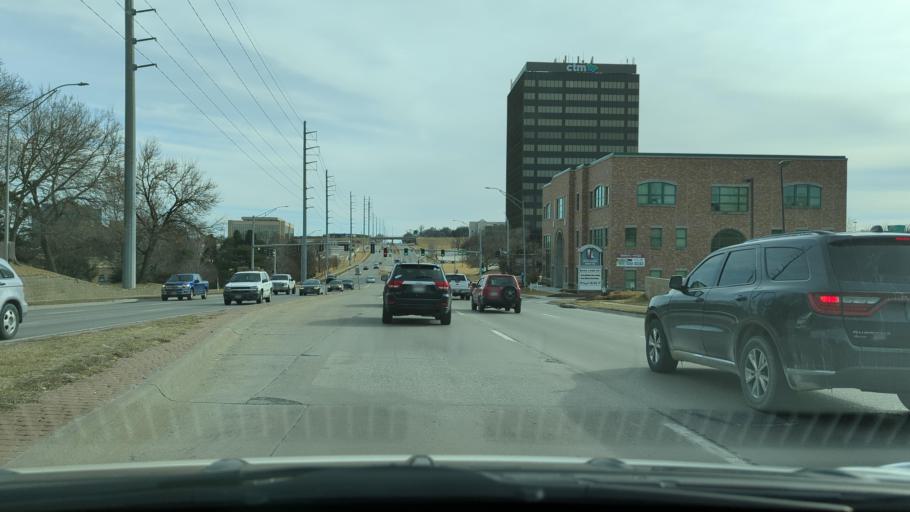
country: US
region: Nebraska
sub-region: Douglas County
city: Ralston
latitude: 41.2414
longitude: -96.0239
